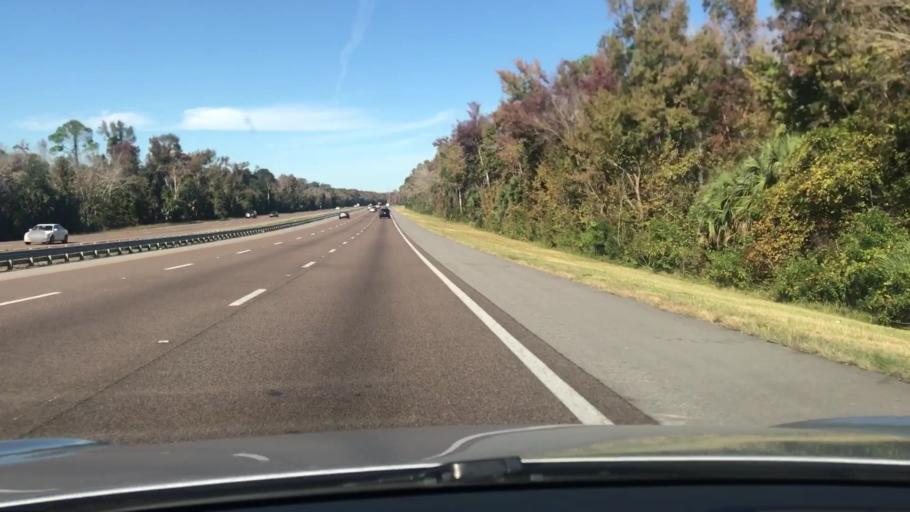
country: US
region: Florida
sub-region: Volusia County
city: Oak Hill
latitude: 28.8362
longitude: -80.9127
